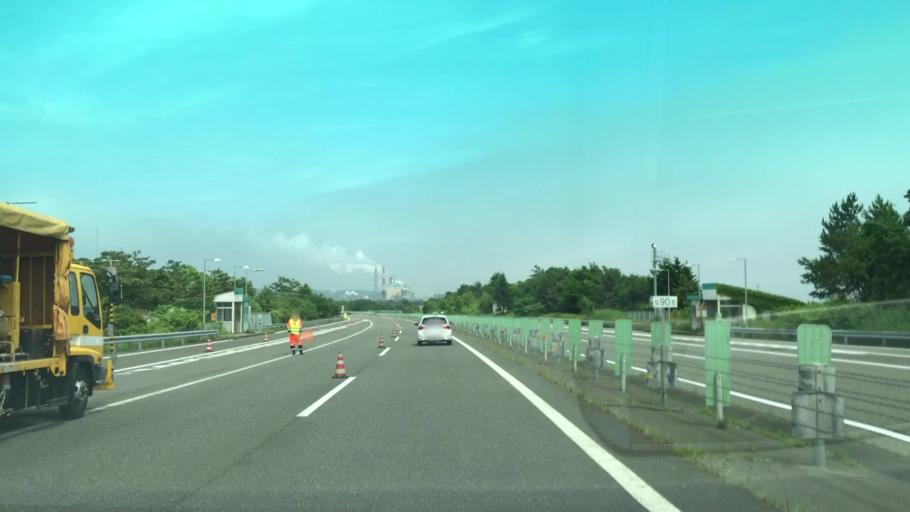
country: JP
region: Hokkaido
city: Shiraoi
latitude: 42.4989
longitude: 141.2612
